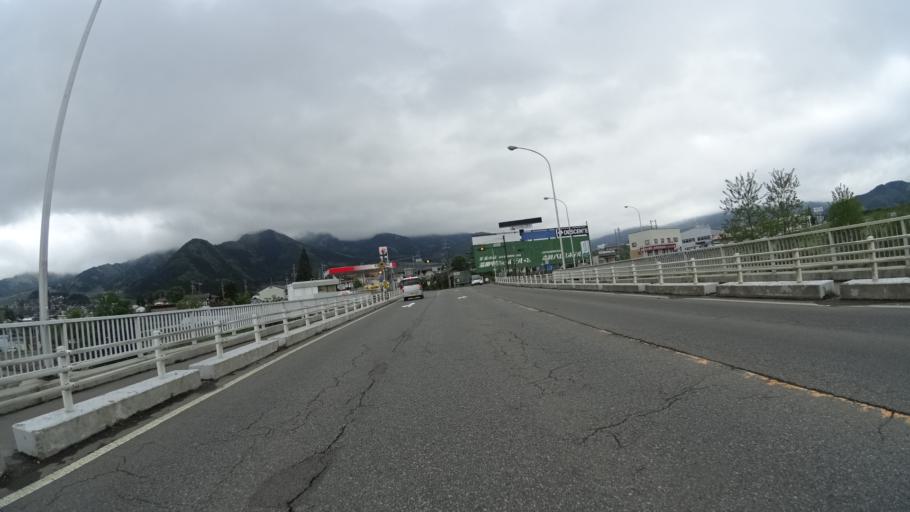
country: JP
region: Nagano
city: Nakano
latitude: 36.7583
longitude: 138.3975
